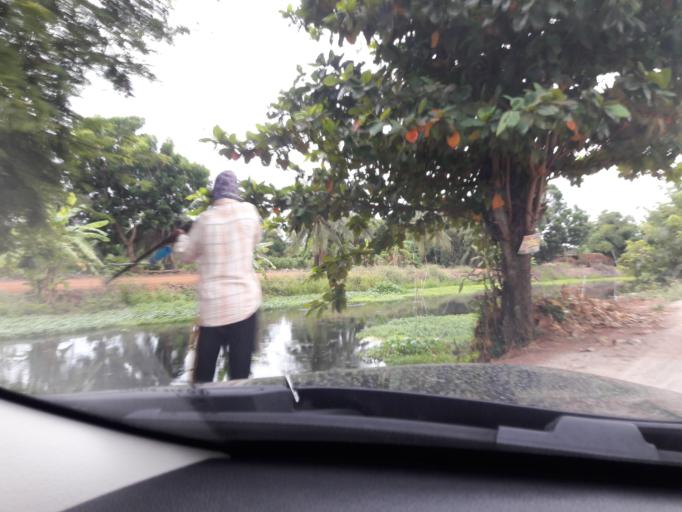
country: TH
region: Ratchaburi
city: Bang Phae
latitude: 13.6135
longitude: 99.9649
